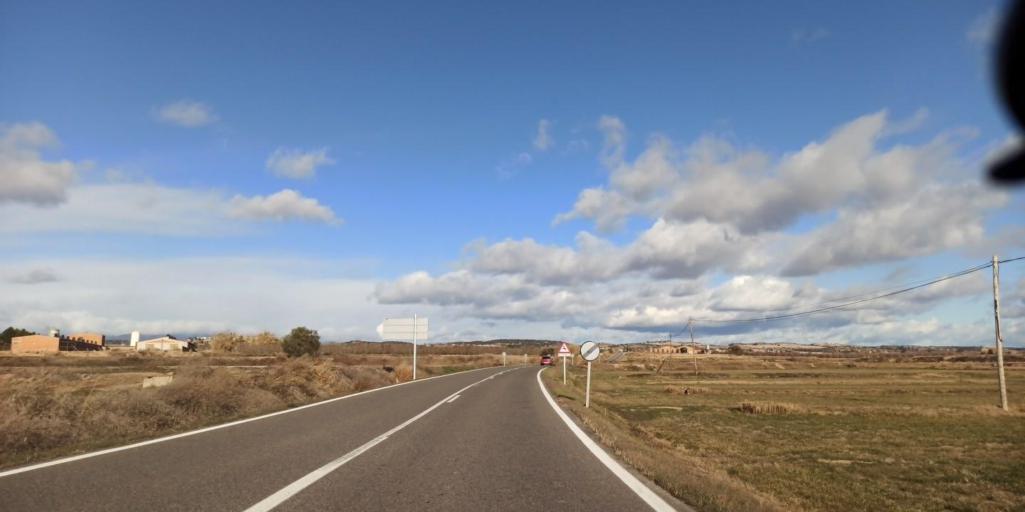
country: ES
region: Catalonia
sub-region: Provincia de Lleida
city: Penelles
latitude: 41.7422
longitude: 0.9487
